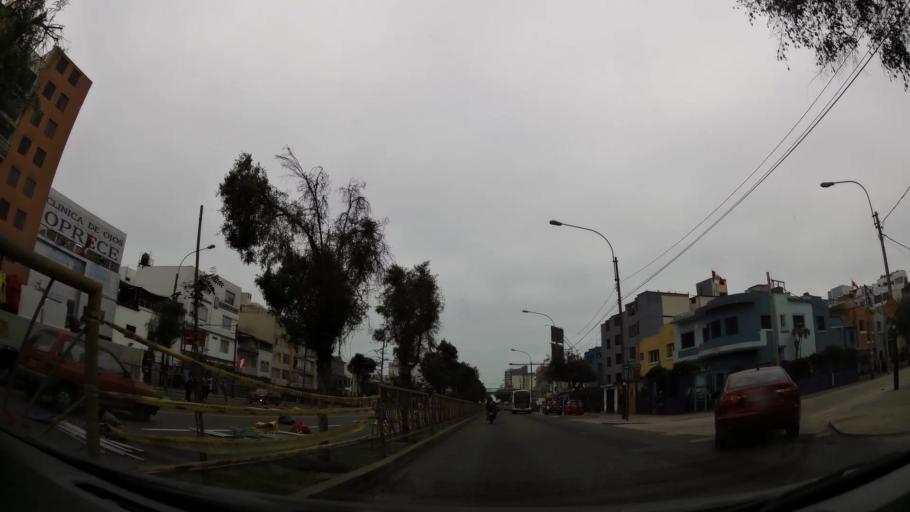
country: PE
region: Lima
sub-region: Lima
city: San Isidro
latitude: -12.0888
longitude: -77.0652
